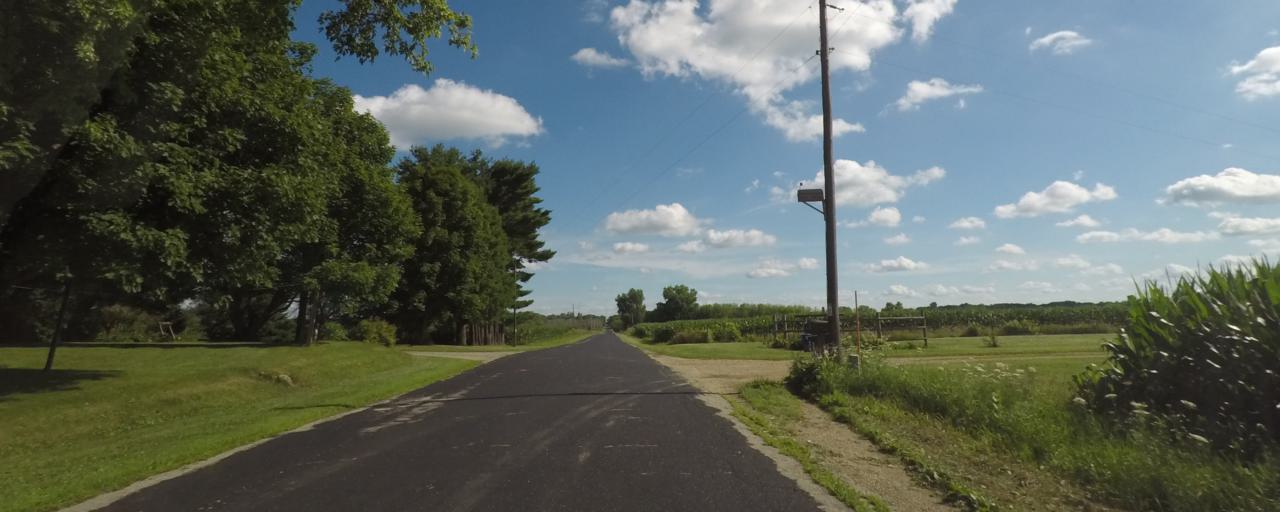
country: US
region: Wisconsin
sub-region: Rock County
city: Edgerton
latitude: 42.8830
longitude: -89.1321
